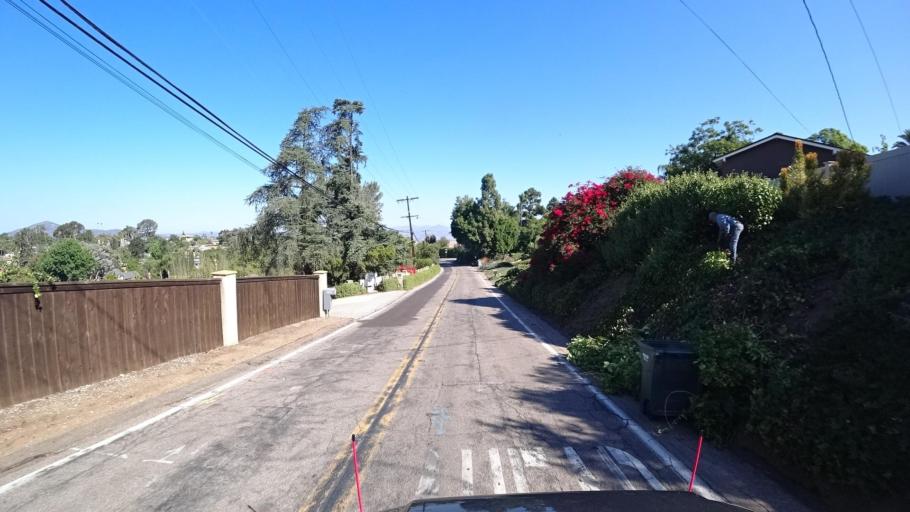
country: US
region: California
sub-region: San Diego County
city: Casa de Oro-Mount Helix
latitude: 32.7720
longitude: -116.9799
